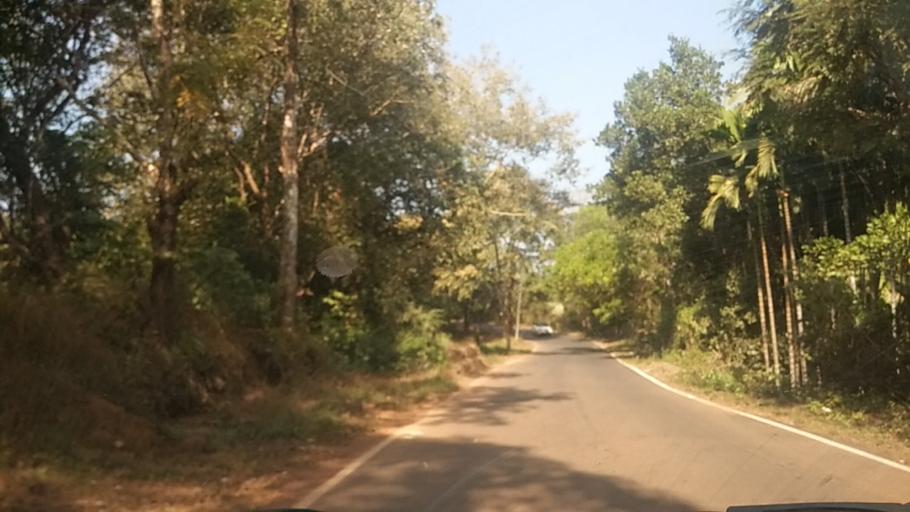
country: IN
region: Goa
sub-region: South Goa
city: Sanguem
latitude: 15.2120
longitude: 74.2129
